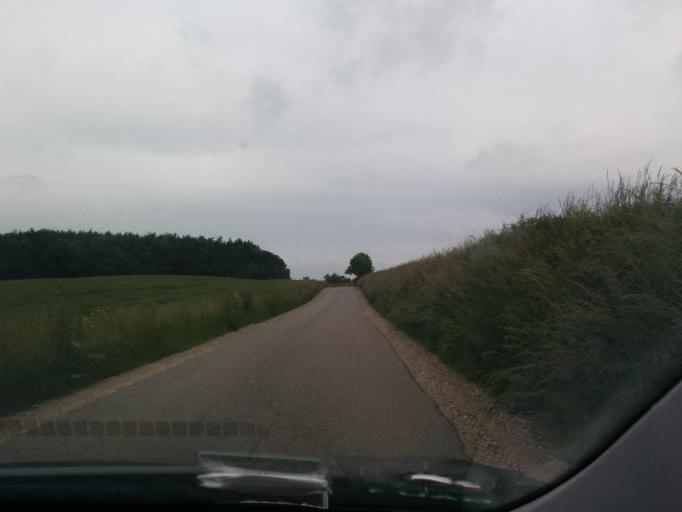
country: DK
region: Central Jutland
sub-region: Syddjurs Kommune
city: Hornslet
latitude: 56.2976
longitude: 10.3757
